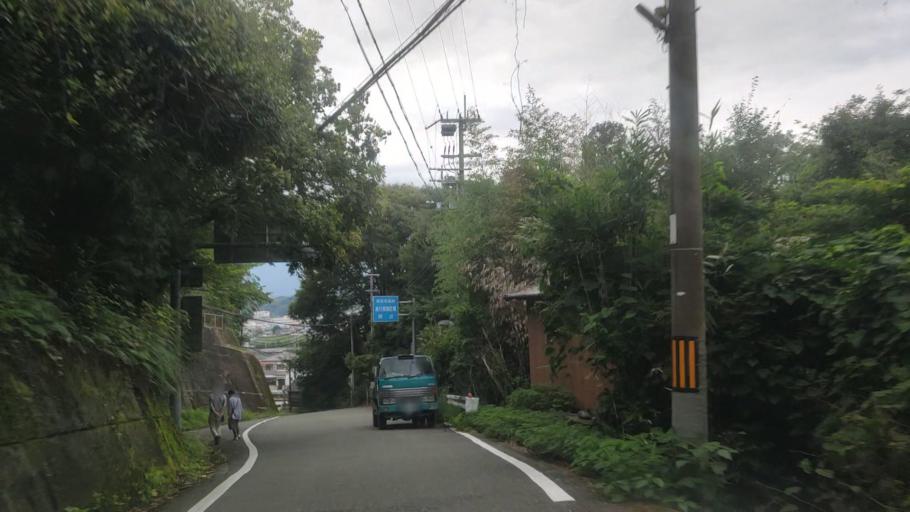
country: JP
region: Wakayama
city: Hashimoto
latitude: 34.3100
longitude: 135.6156
